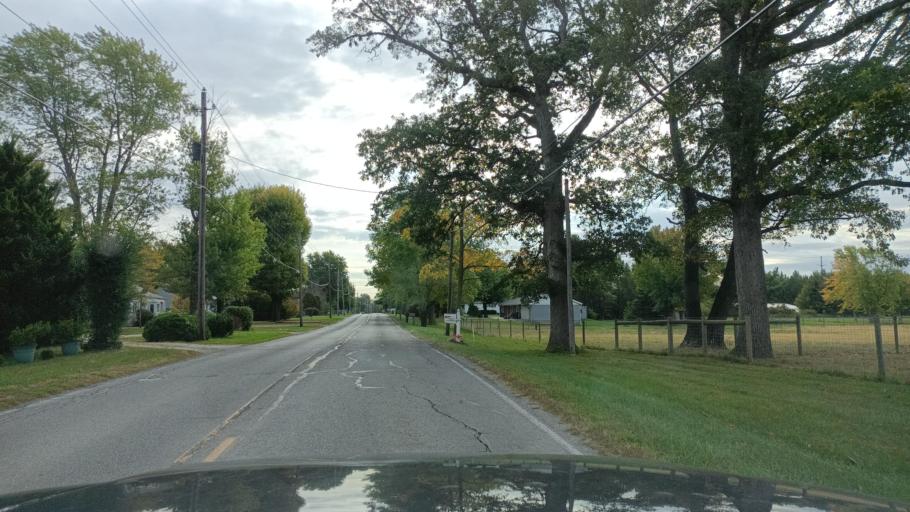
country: US
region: Indiana
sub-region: Delaware County
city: Yorktown
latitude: 40.2038
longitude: -85.4564
